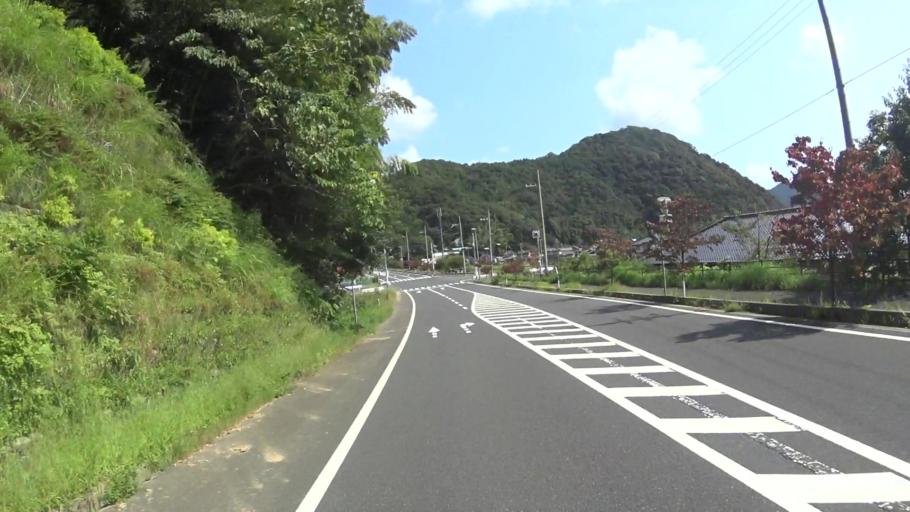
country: JP
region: Kyoto
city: Miyazu
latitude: 35.6670
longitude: 135.2649
